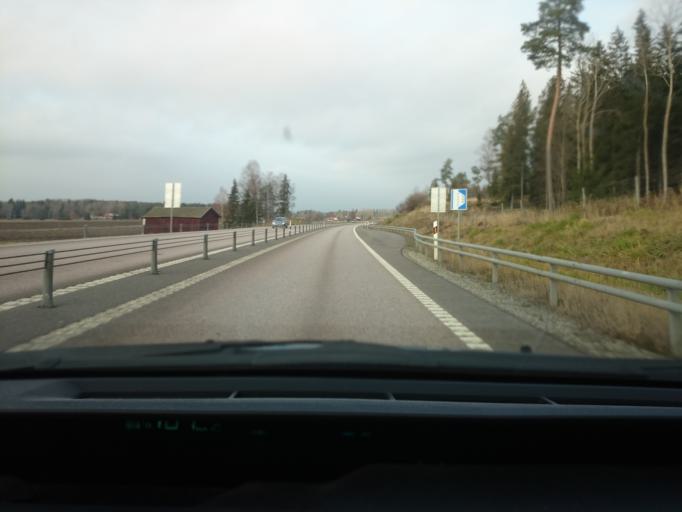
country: SE
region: Vaestmanland
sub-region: Sala Kommun
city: Sala
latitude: 59.9006
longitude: 16.5383
